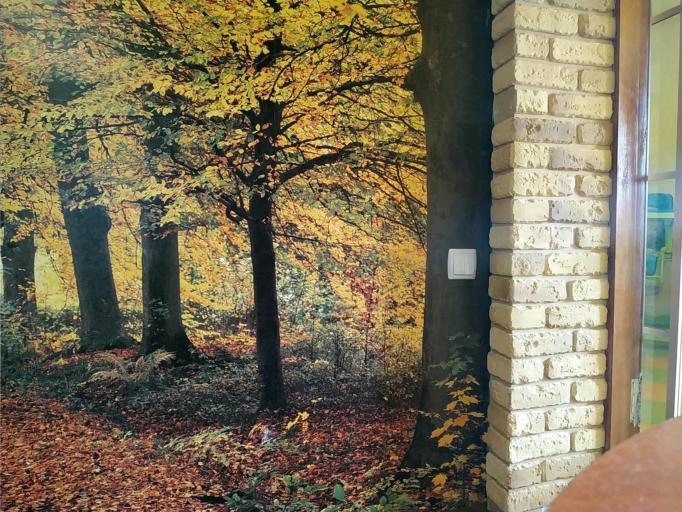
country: RU
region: Smolensk
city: Katyn'
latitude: 54.9061
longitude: 31.7753
